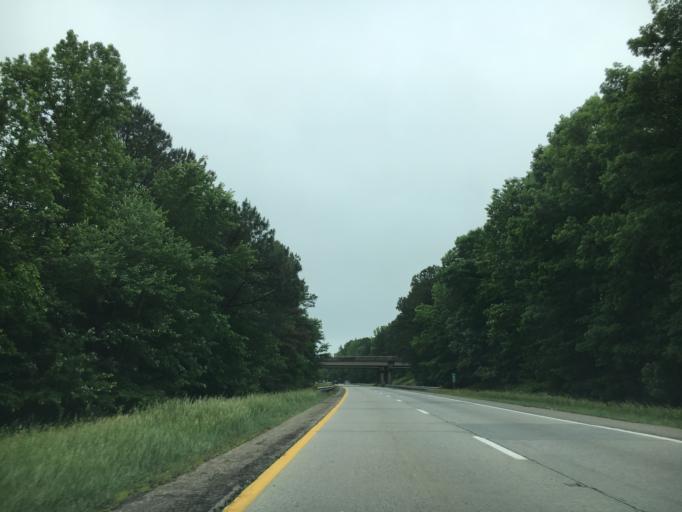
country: US
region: Virginia
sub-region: Chesterfield County
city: Matoaca
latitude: 37.1880
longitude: -77.4903
